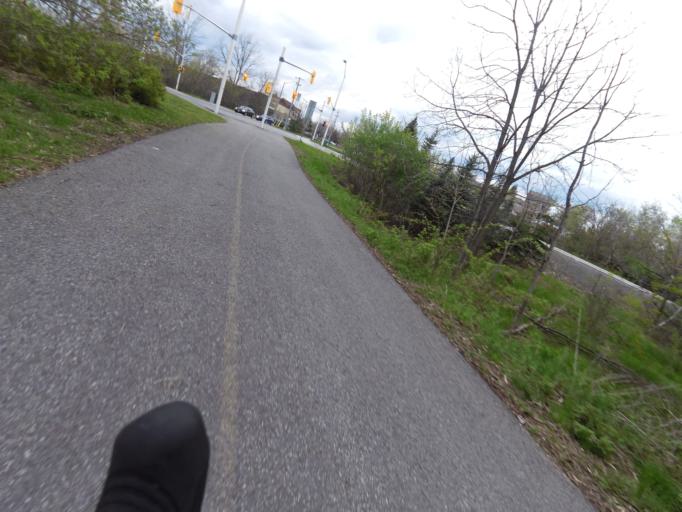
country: CA
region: Ontario
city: Bells Corners
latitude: 45.2759
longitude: -75.7465
